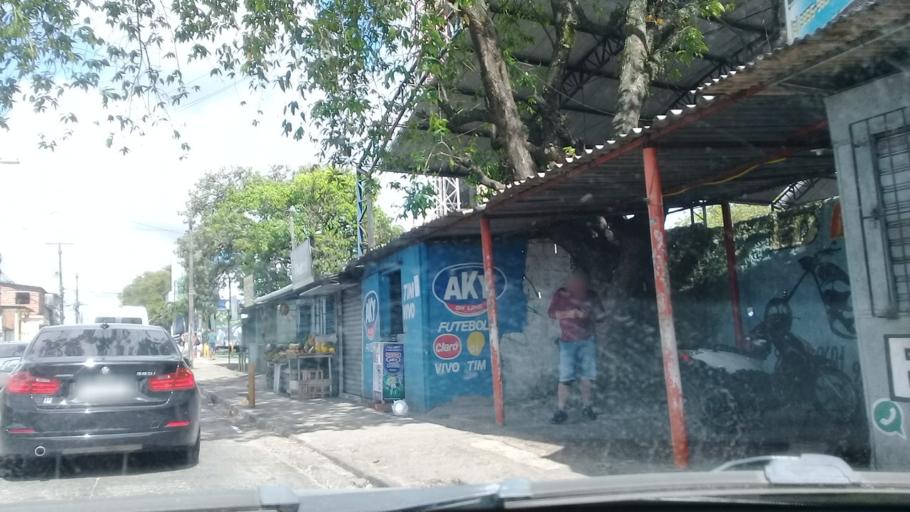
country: BR
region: Pernambuco
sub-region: Jaboatao Dos Guararapes
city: Jaboatao dos Guararapes
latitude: -8.1153
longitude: -34.9488
